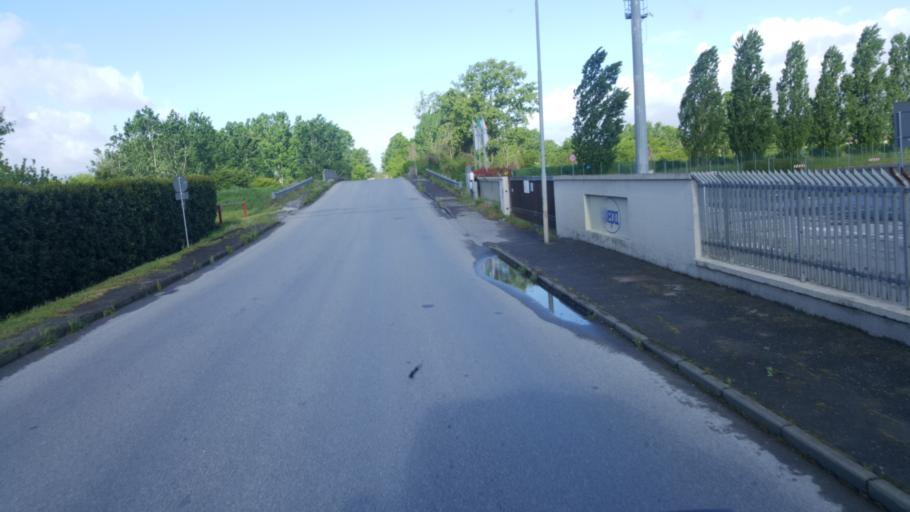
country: IT
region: Tuscany
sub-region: Provincia di Lucca
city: Porcari
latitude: 43.8498
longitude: 10.5967
